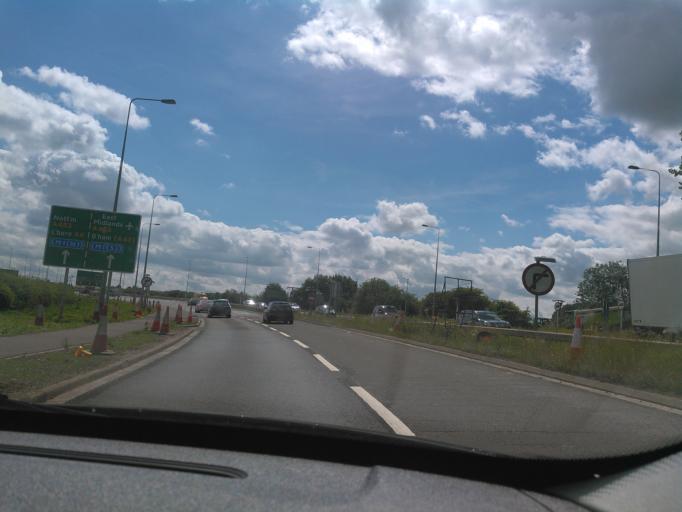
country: GB
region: England
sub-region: Leicestershire
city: Kegworth
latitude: 52.8469
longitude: -1.2993
